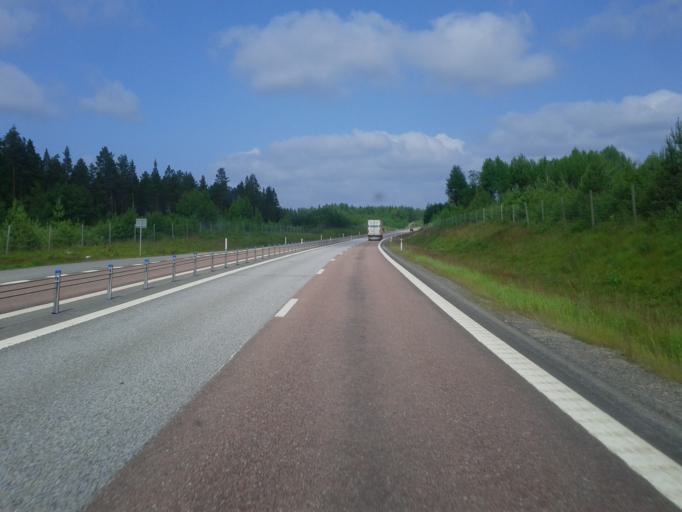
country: SE
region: Vaesterbotten
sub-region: Skelleftea Kommun
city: Skelleftea
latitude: 64.7030
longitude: 21.0012
